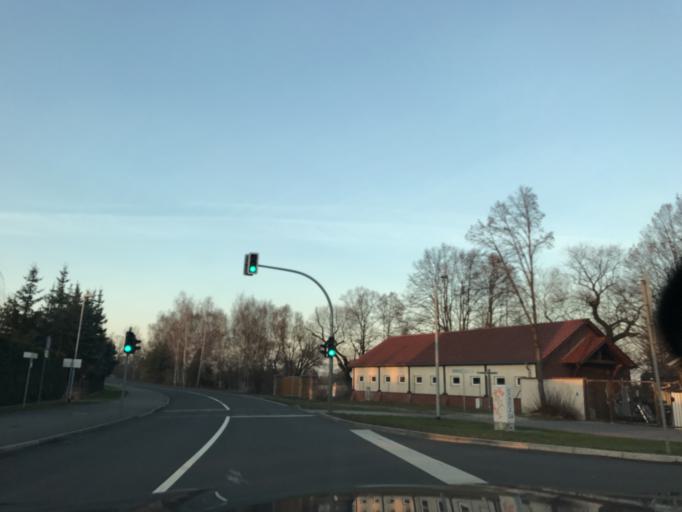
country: DE
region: Brandenburg
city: Brandenburg an der Havel
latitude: 52.4890
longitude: 12.4622
